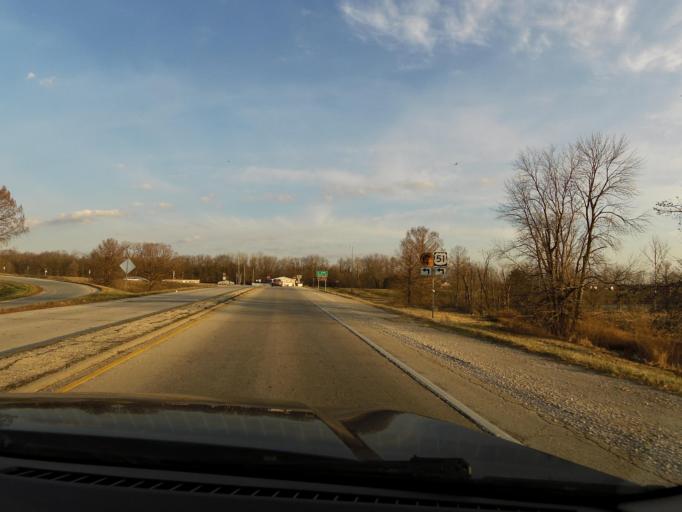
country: US
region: Illinois
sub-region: Fayette County
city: Vandalia
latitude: 38.9587
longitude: -89.0847
